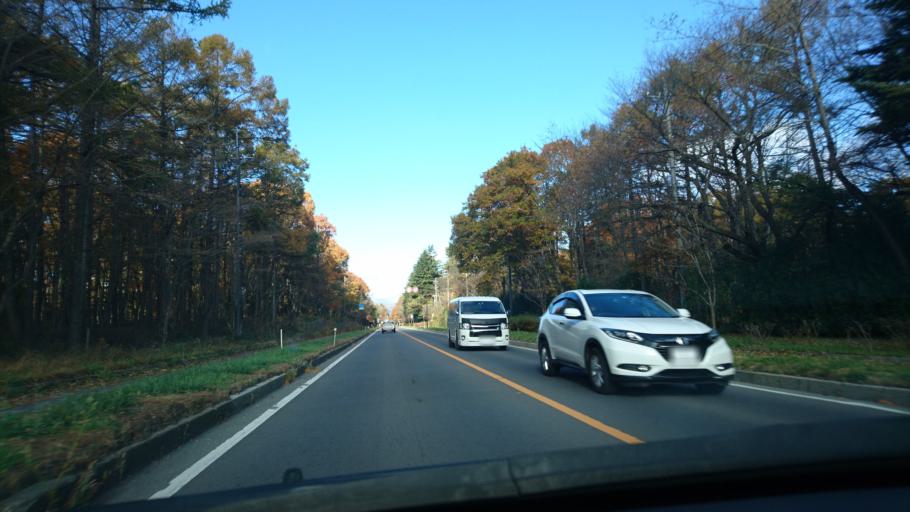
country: JP
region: Nagano
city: Saku
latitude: 36.3255
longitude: 138.6198
